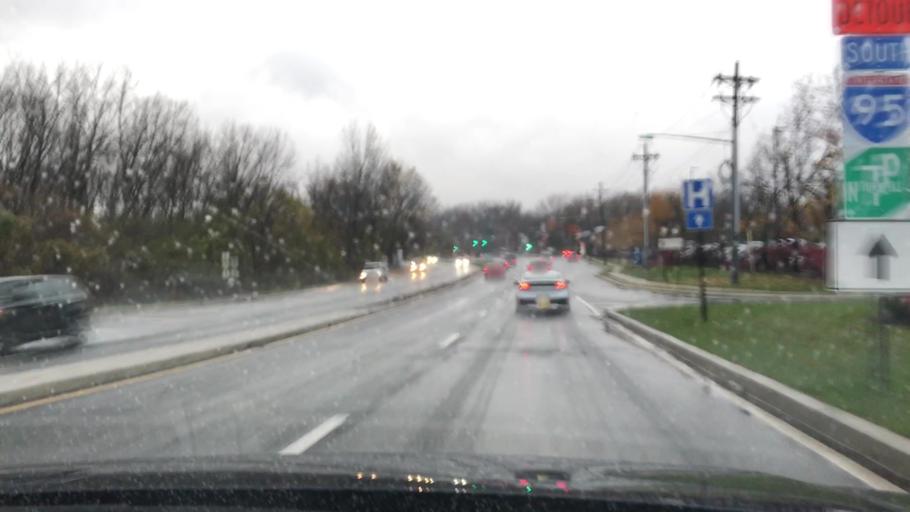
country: US
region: New Jersey
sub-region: Bergen County
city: Leonia
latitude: 40.8702
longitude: -74.0045
